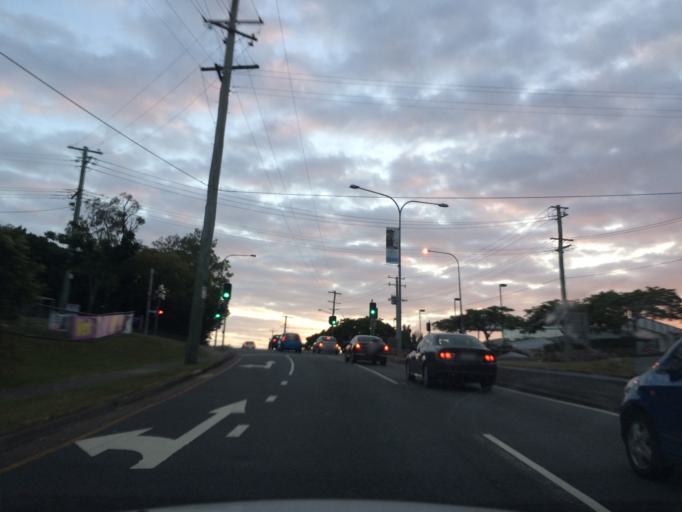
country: AU
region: Queensland
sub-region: Brisbane
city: Taringa
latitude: -27.5011
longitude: 152.9658
